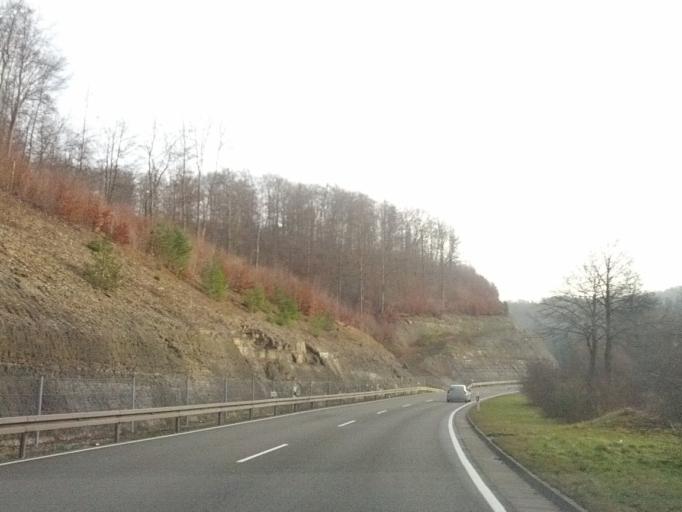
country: DE
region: Thuringia
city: Utendorf
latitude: 50.5872
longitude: 10.4512
